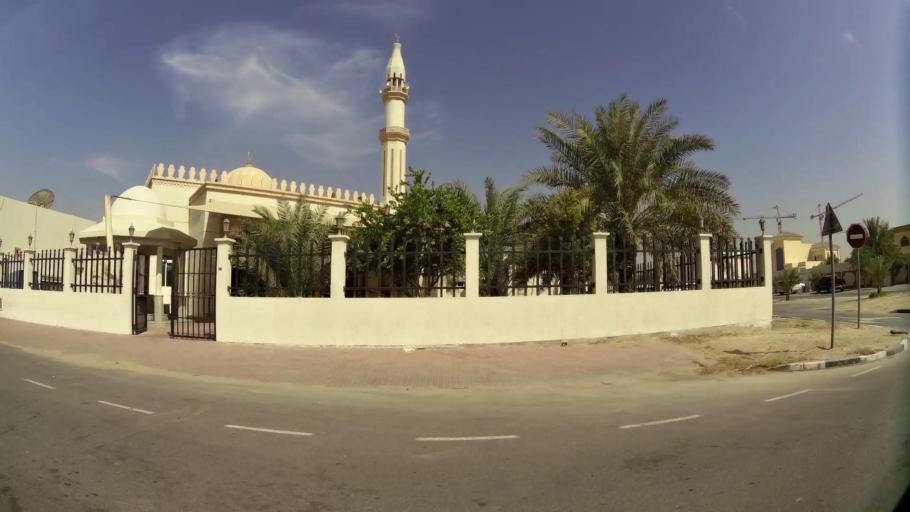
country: AE
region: Ash Shariqah
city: Sharjah
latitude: 25.2722
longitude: 55.4093
